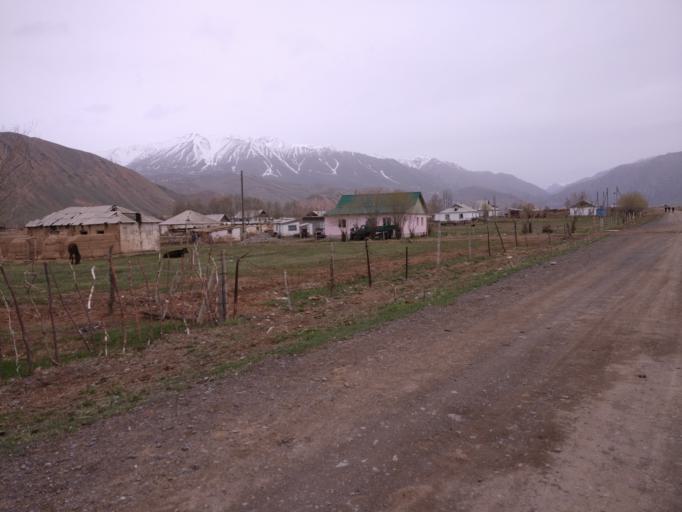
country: KG
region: Naryn
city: Naryn
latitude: 41.5175
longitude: 76.4406
